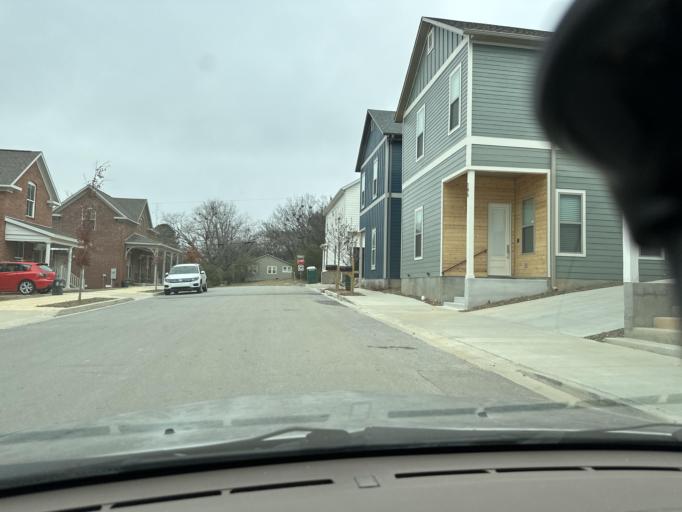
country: US
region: Arkansas
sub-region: Washington County
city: Fayetteville
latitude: 36.0593
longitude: -94.1573
